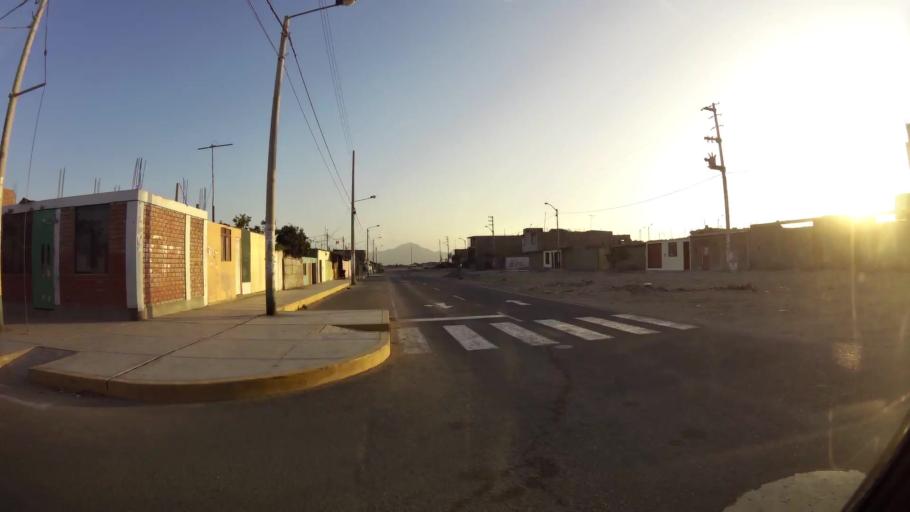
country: PE
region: Ancash
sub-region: Provincia de Santa
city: Buenos Aires
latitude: -9.1486
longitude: -78.5066
